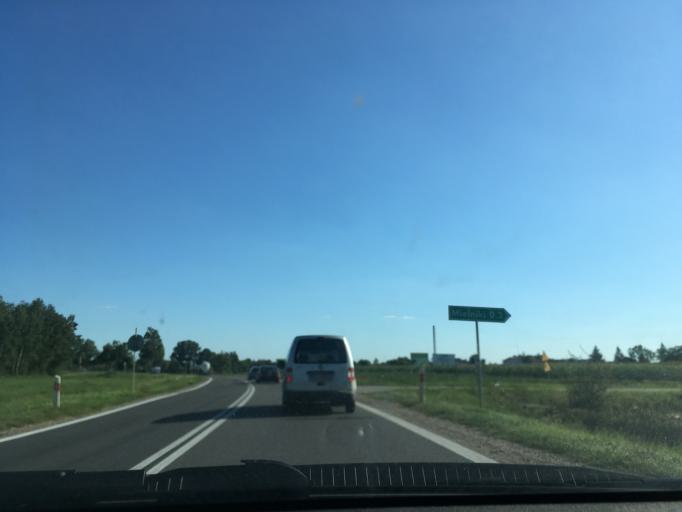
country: PL
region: Podlasie
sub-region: Powiat sokolski
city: Suchowola
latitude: 53.4529
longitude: 23.0873
